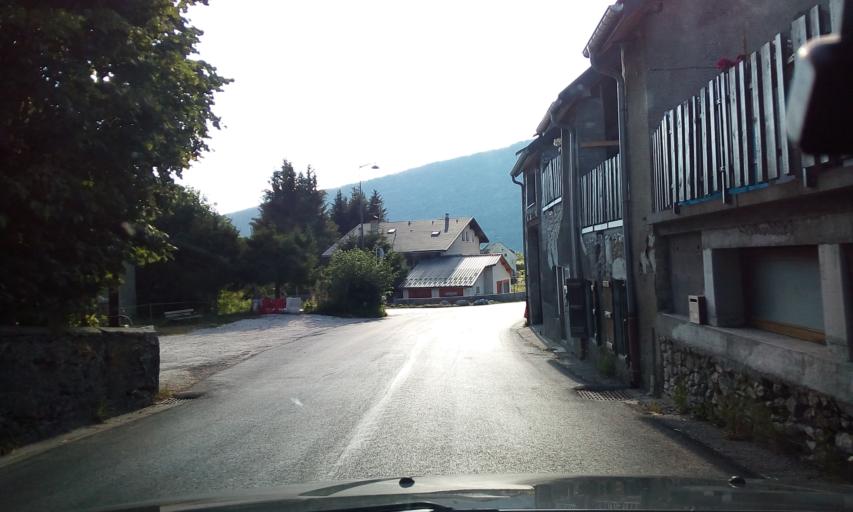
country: FR
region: Rhone-Alpes
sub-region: Departement de l'Isere
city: Lans-en-Vercors
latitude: 45.1264
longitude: 5.5961
